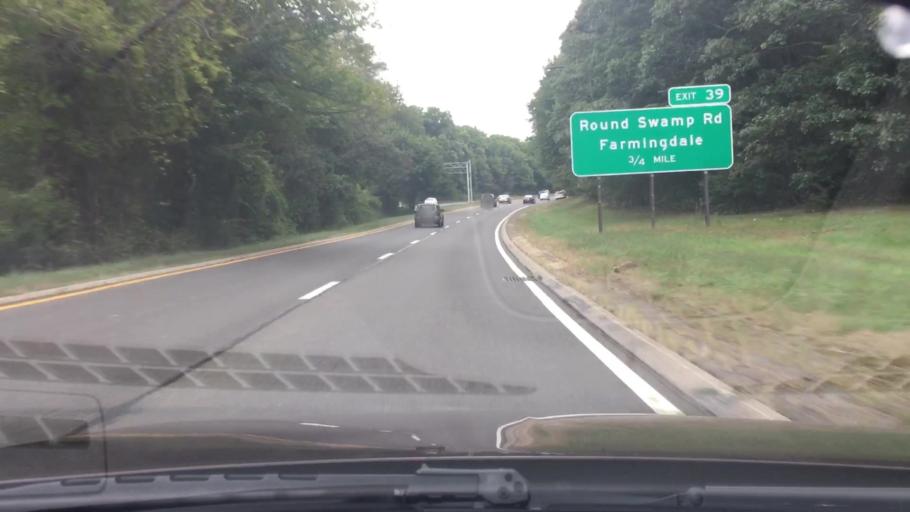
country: US
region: New York
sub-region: Nassau County
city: Woodbury
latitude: 40.8042
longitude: -73.4573
